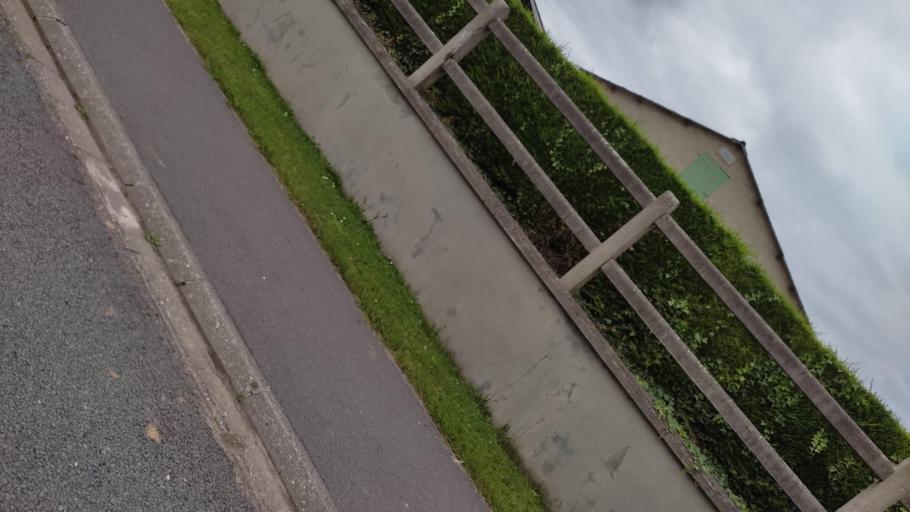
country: FR
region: Nord-Pas-de-Calais
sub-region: Departement du Pas-de-Calais
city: Beaumetz-les-Loges
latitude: 50.2568
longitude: 2.6436
